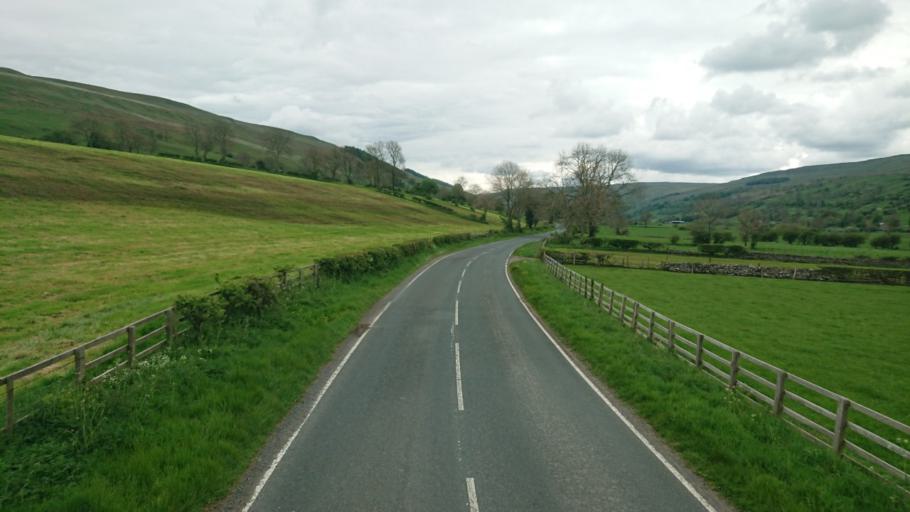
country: GB
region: England
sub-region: North Yorkshire
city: Leyburn
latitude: 54.2670
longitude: -2.0108
